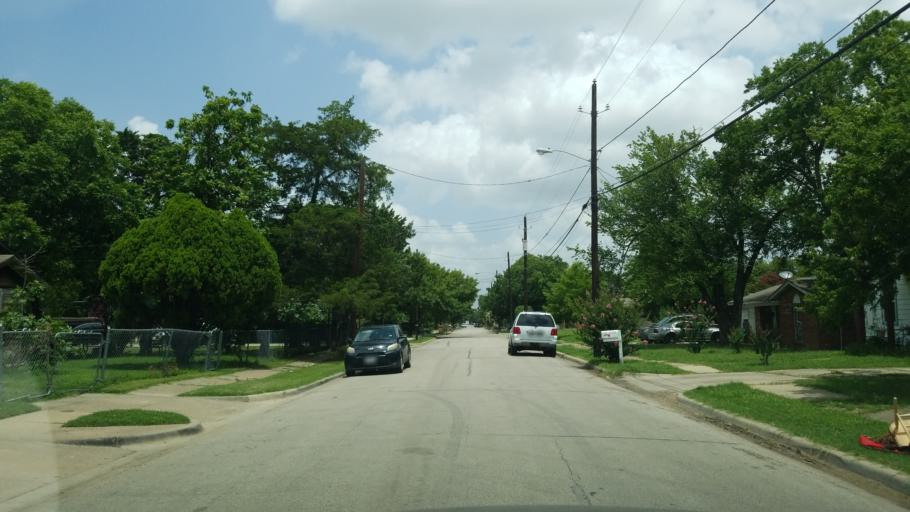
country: US
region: Texas
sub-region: Dallas County
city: Cockrell Hill
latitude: 32.7863
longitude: -96.9014
